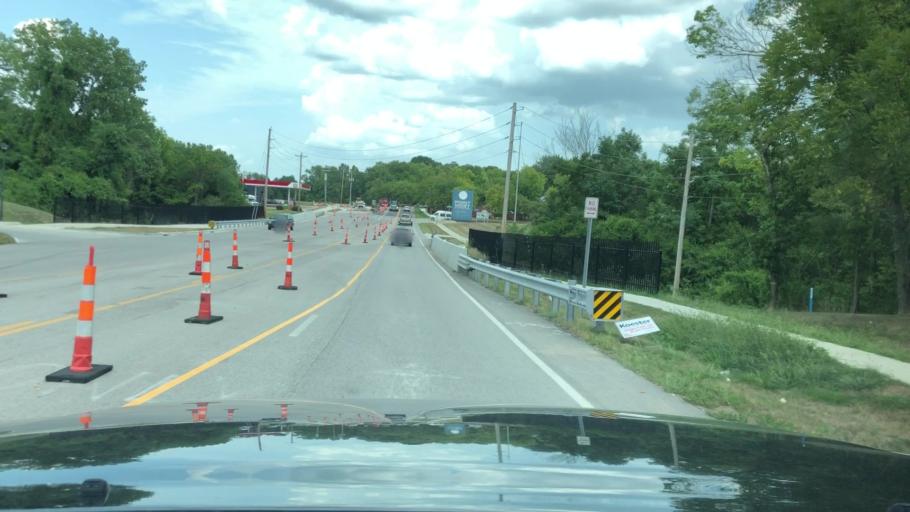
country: US
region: Missouri
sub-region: Saint Charles County
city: Saint Peters
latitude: 38.7967
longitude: -90.5612
